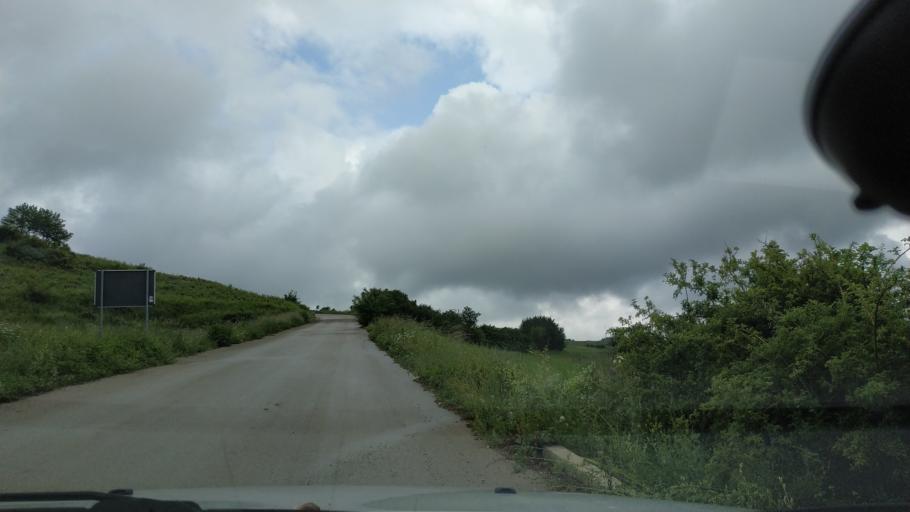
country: RS
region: Central Serbia
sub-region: Toplicki Okrug
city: Prokuplje
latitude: 43.4035
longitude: 21.5590
